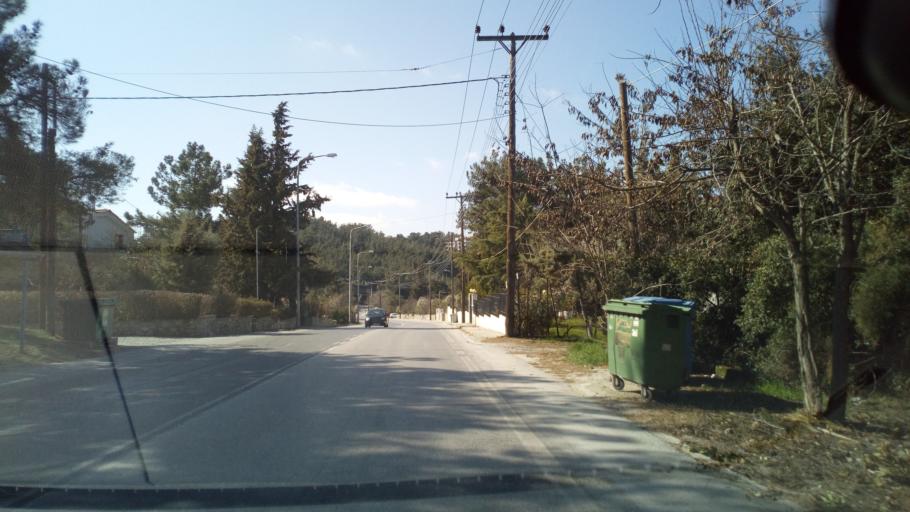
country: GR
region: Central Macedonia
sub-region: Nomos Thessalonikis
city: Panorama
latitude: 40.5950
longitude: 23.0469
